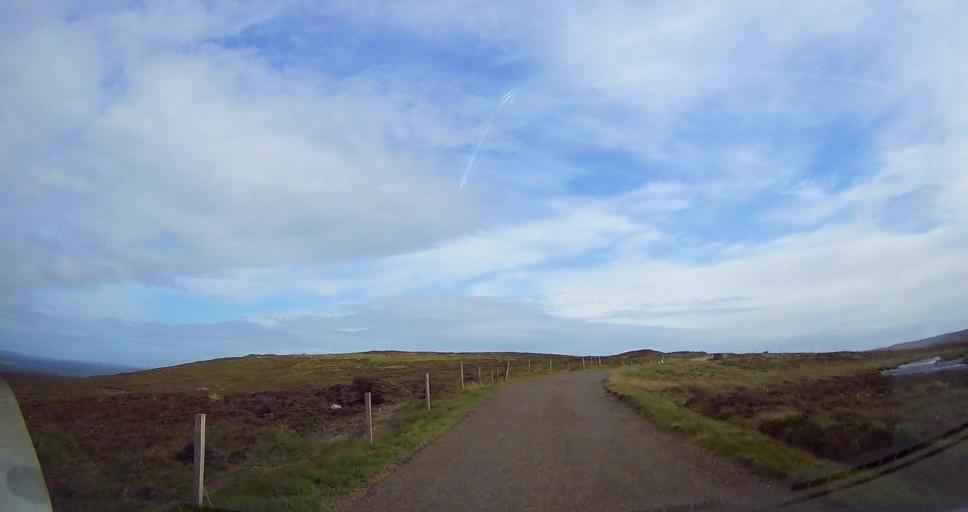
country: GB
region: Scotland
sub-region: Orkney Islands
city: Stromness
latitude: 58.8816
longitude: -3.2484
